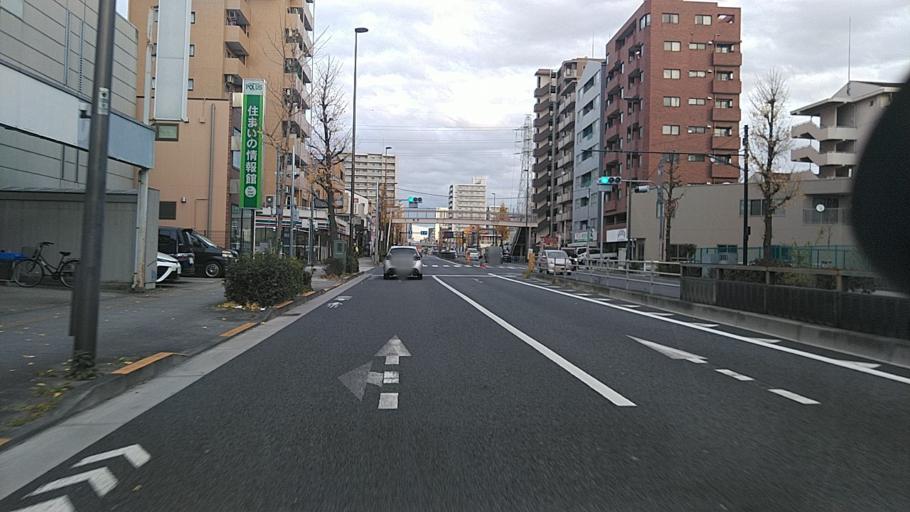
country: JP
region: Saitama
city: Soka
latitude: 35.7712
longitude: 139.8034
